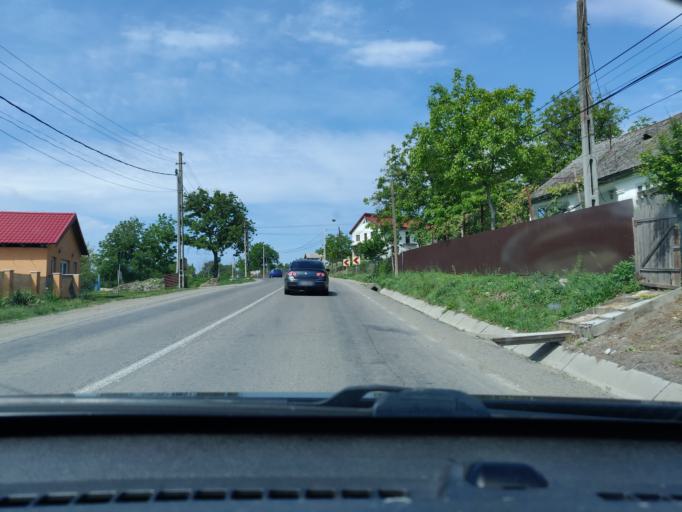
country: RO
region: Vrancea
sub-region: Comuna Vidra
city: Vidra
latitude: 45.9107
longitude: 26.9207
